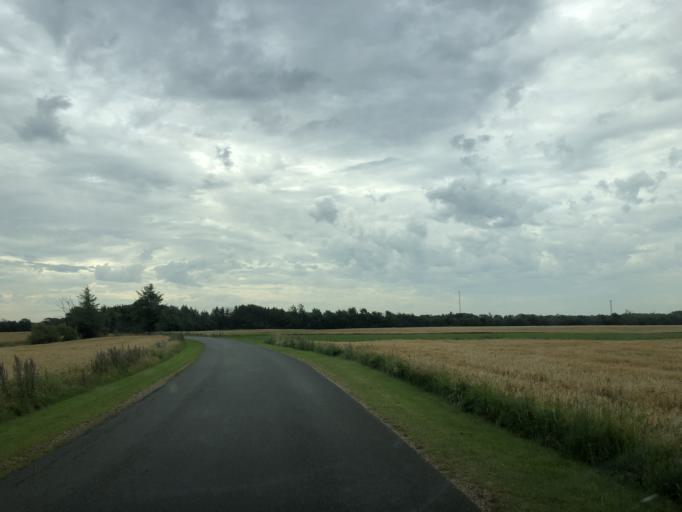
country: DK
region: Central Jutland
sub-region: Holstebro Kommune
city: Holstebro
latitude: 56.3819
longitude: 8.5211
